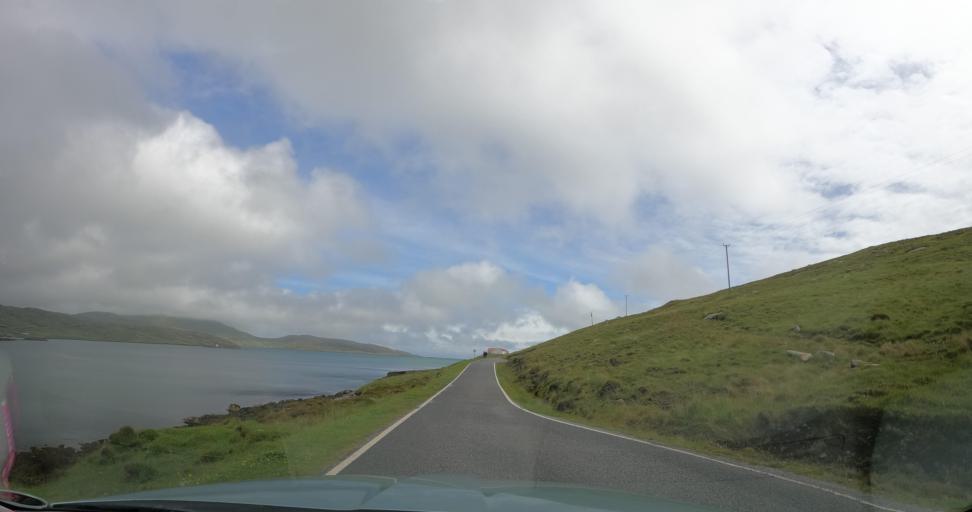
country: GB
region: Scotland
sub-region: Eilean Siar
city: Barra
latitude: 56.9372
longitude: -7.5284
